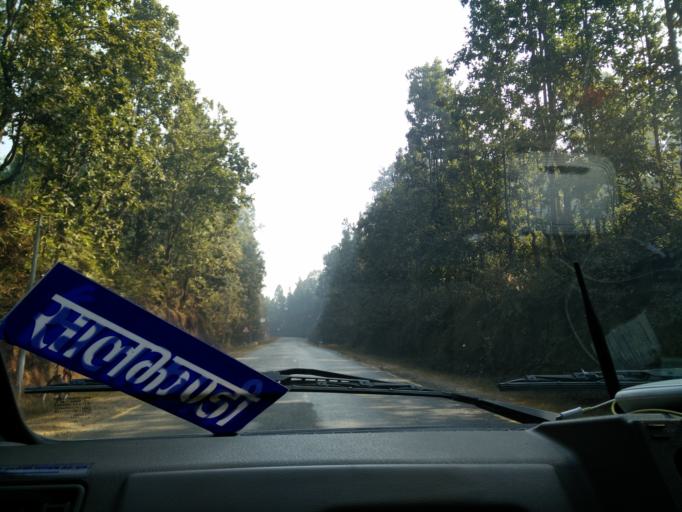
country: NP
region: Central Region
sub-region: Narayani Zone
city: Bharatpur
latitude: 27.6174
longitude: 84.0222
